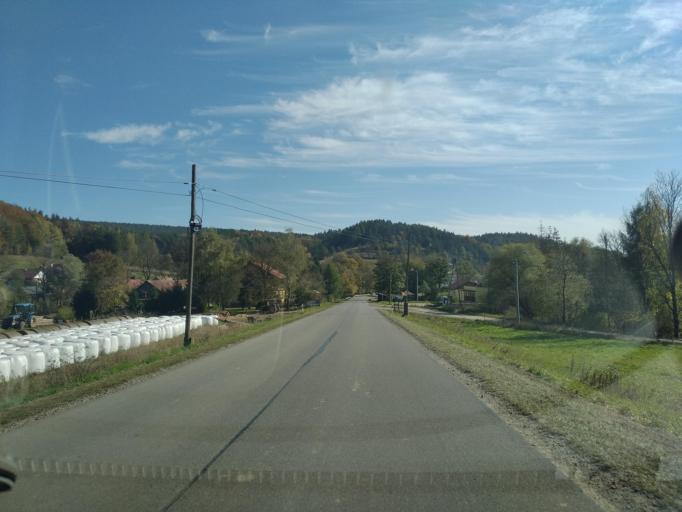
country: PL
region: Subcarpathian Voivodeship
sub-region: Powiat sanocki
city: Komancza
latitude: 49.3593
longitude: 22.0233
